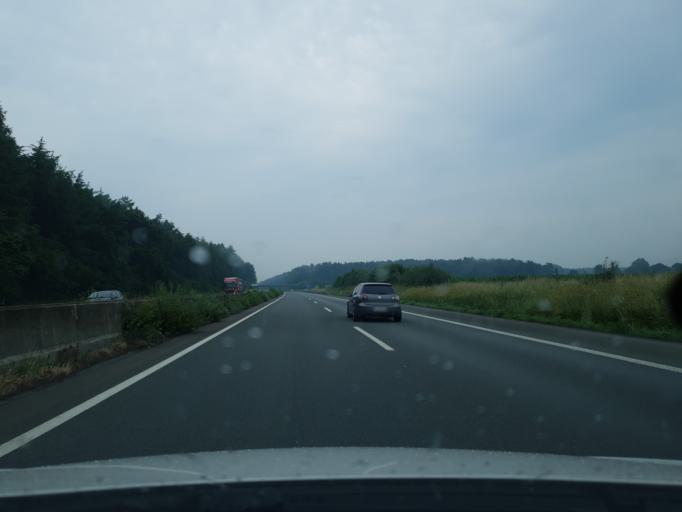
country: DE
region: North Rhine-Westphalia
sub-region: Regierungsbezirk Munster
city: Klein Reken
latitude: 51.8363
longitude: 7.0036
